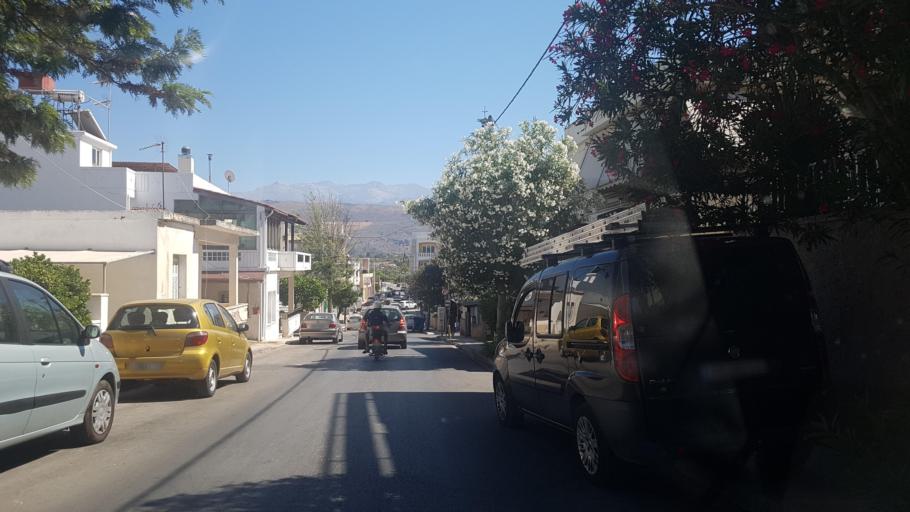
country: GR
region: Crete
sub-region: Nomos Chanias
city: Chania
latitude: 35.5054
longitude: 24.0178
